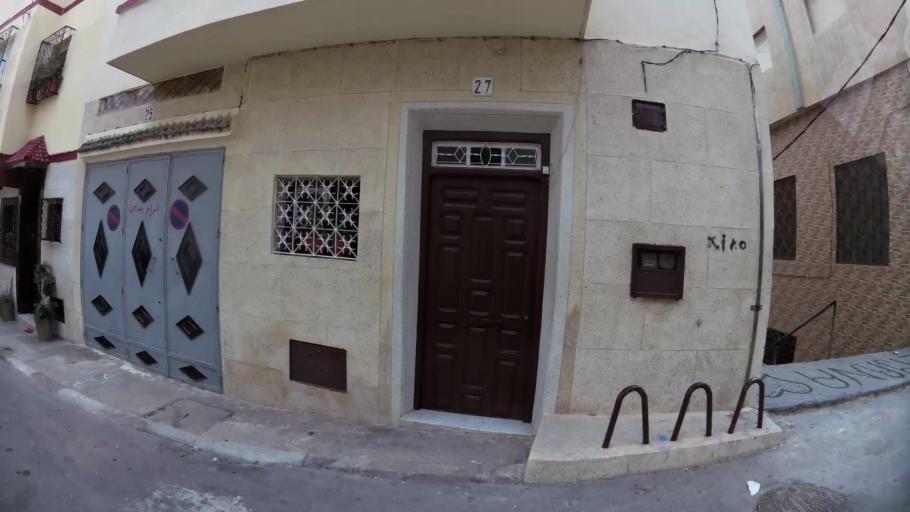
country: MA
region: Tanger-Tetouan
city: Tetouan
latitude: 35.5769
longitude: -5.3611
